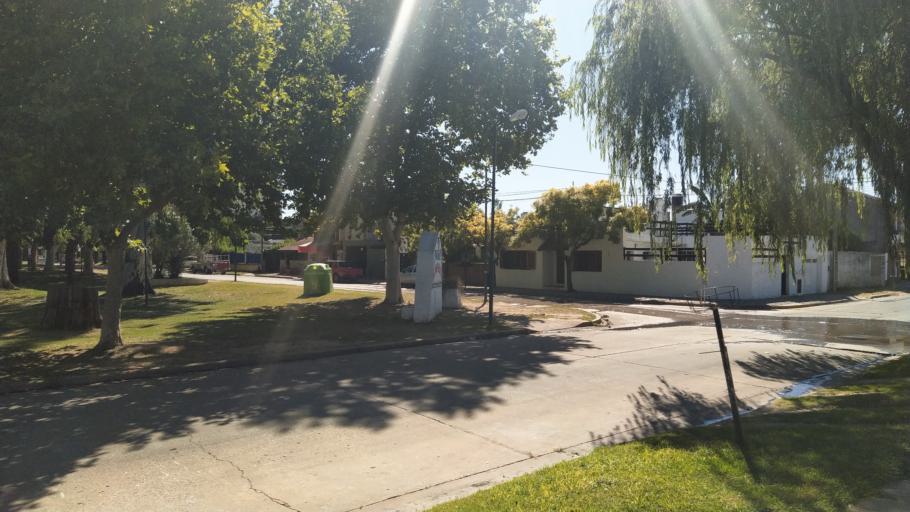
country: AR
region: Buenos Aires
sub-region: Partido de Salto
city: Salto
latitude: -34.2862
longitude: -60.2563
